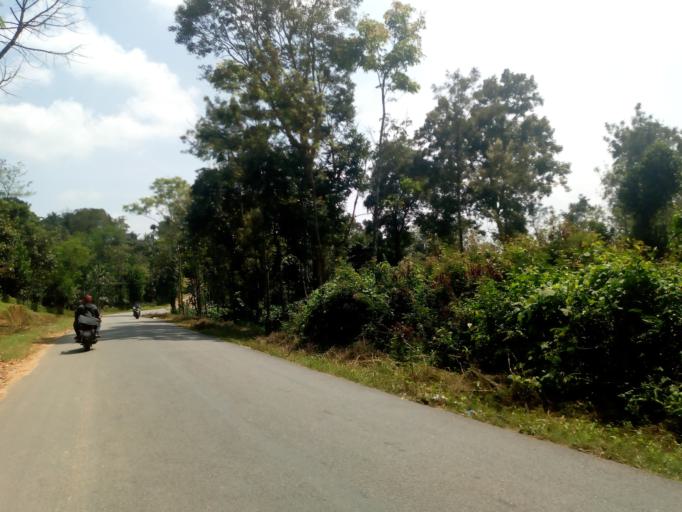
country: IN
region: Karnataka
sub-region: Kodagu
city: Ponnampet
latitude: 12.0669
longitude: 75.9450
